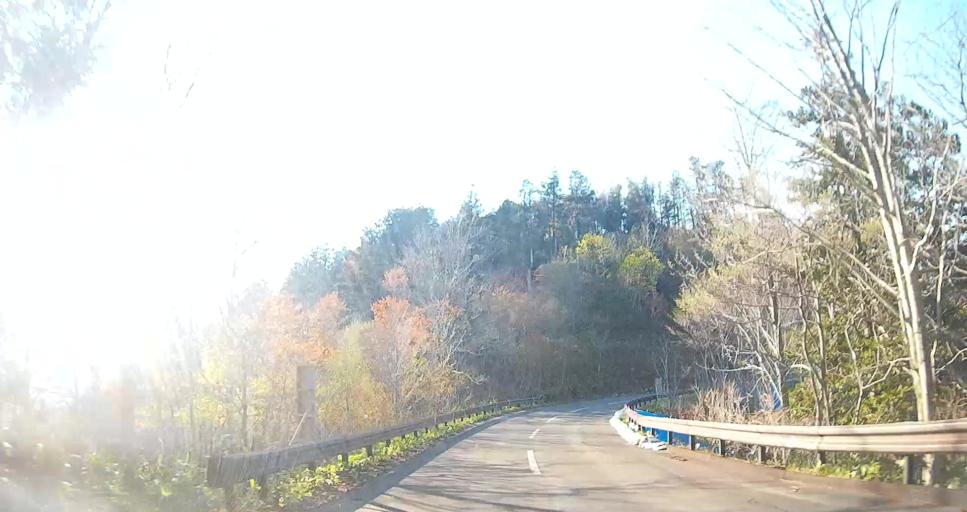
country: JP
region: Aomori
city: Mutsu
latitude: 41.3095
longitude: 141.1131
